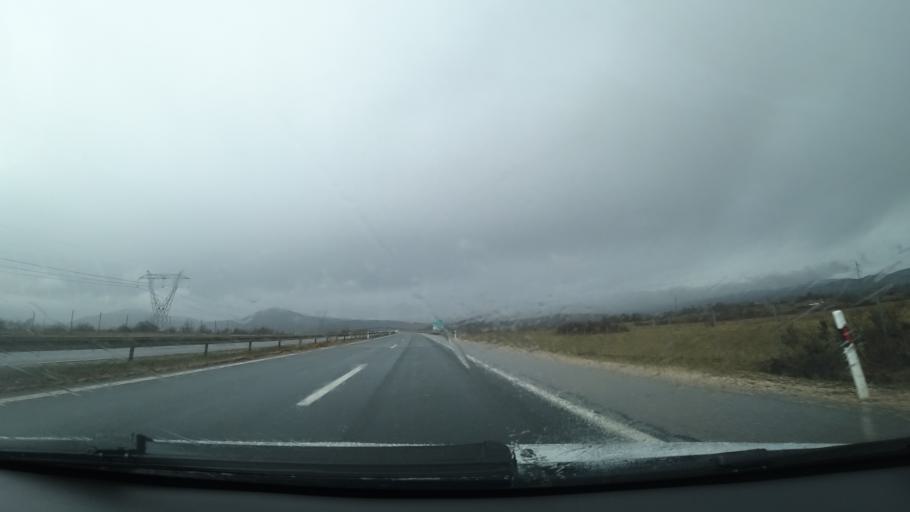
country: HR
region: Licko-Senjska
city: Gospic
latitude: 44.6112
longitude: 15.4401
